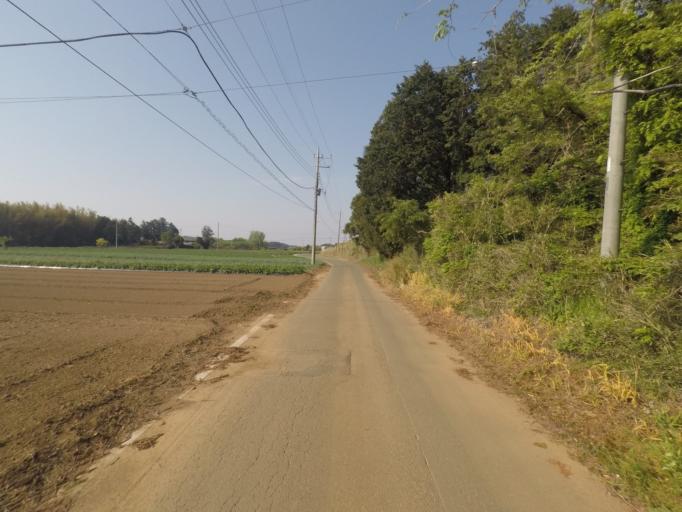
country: JP
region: Ibaraki
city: Itako
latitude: 36.0687
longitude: 140.4536
